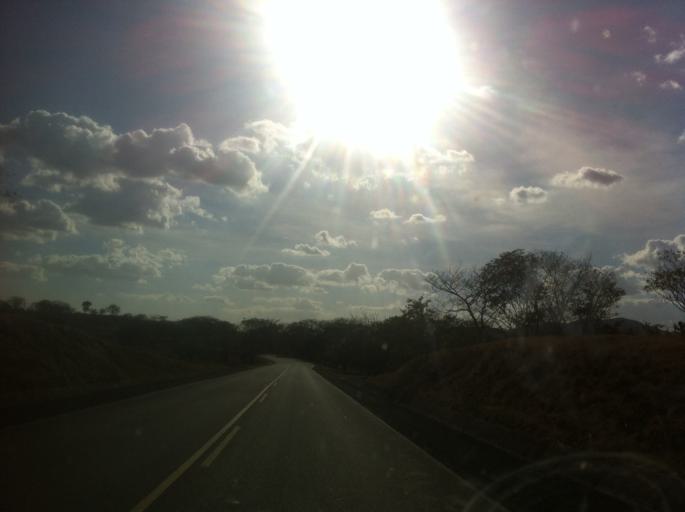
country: NI
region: Chontales
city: Acoyapa
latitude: 11.9915
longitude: -85.1665
